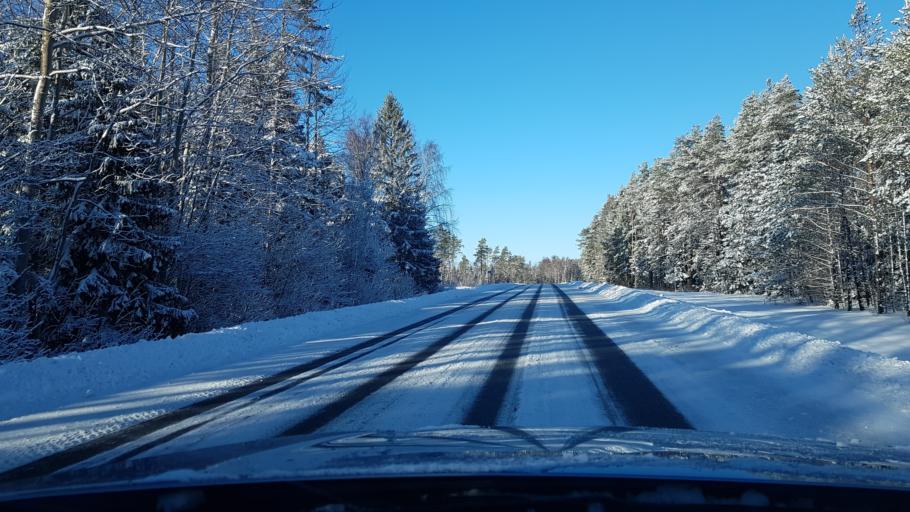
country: EE
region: Hiiumaa
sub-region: Kaerdla linn
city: Kardla
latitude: 58.9681
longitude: 22.7714
